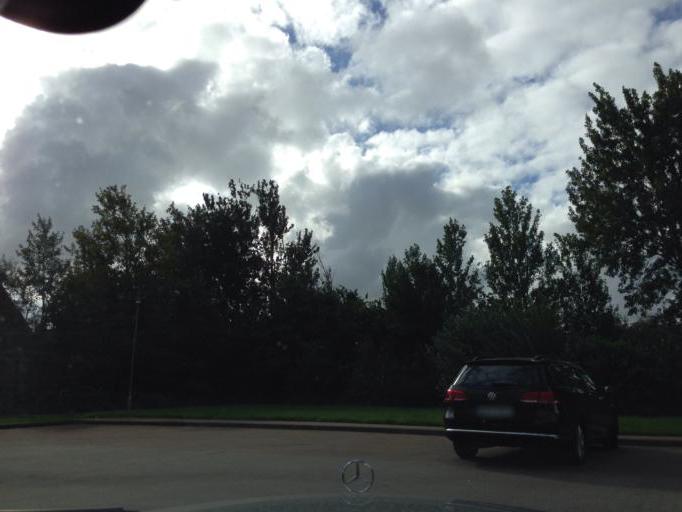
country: DE
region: Schleswig-Holstein
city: Wyk auf Fohr
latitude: 54.6936
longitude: 8.5674
